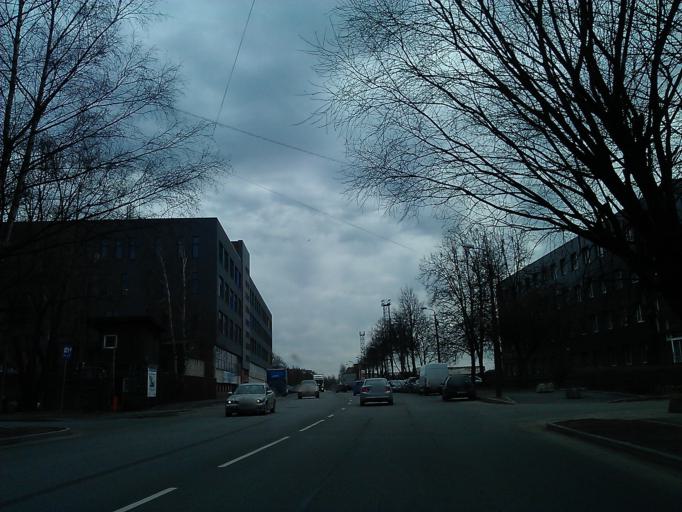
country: LV
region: Riga
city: Riga
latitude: 56.9628
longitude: 24.1651
